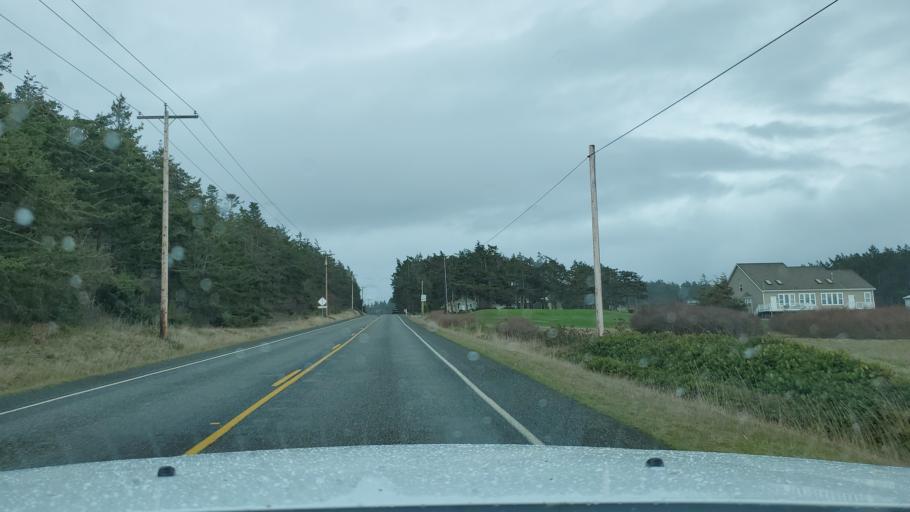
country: US
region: Washington
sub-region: Island County
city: Ault Field
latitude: 48.3078
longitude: -122.7123
